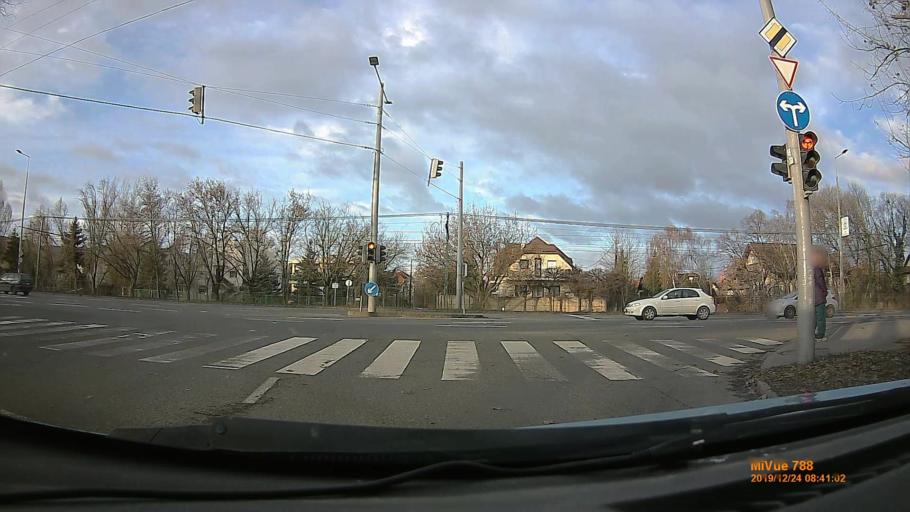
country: HU
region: Borsod-Abauj-Zemplen
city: Tarcal
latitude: 48.1424
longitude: 21.3348
